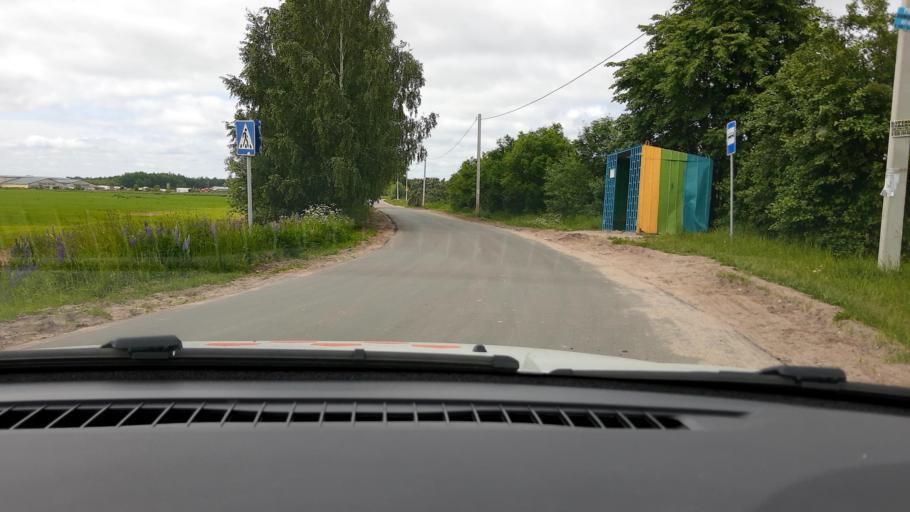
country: RU
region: Nizjnij Novgorod
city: Sitniki
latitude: 56.5170
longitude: 44.1121
